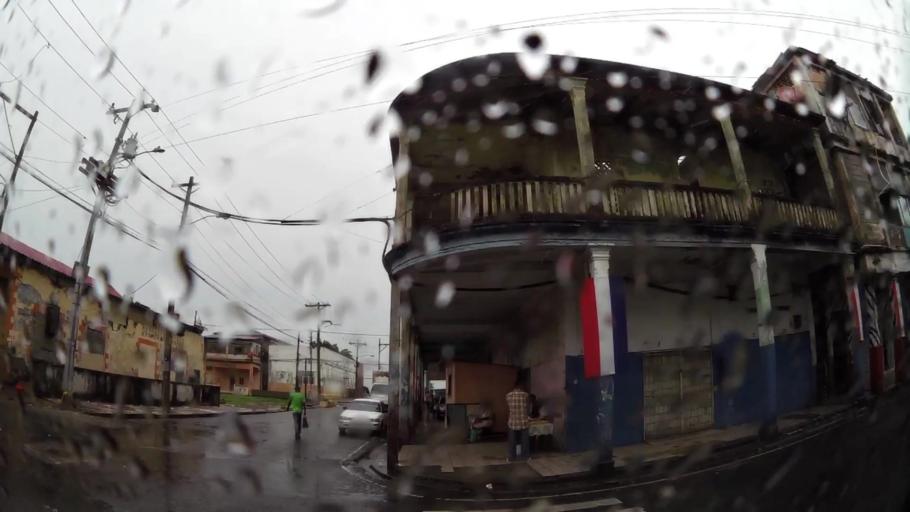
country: PA
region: Colon
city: Colon
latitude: 9.3592
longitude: -79.9043
